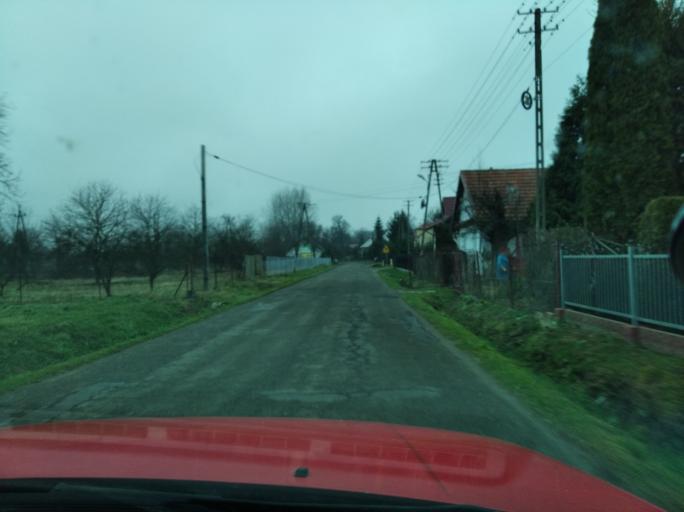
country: PL
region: Subcarpathian Voivodeship
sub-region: Powiat przeworski
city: Mirocin
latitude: 50.0430
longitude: 22.5555
